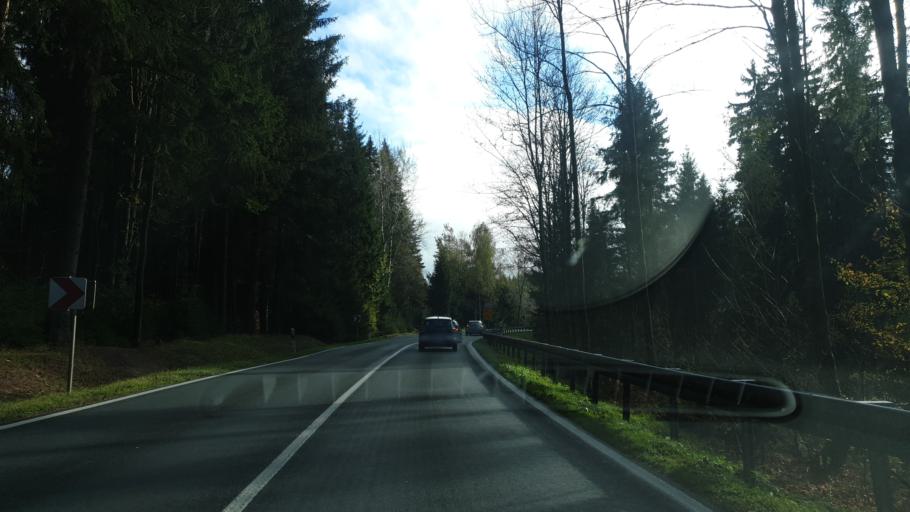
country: DE
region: Saxony
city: Eibenstock
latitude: 50.5107
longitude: 12.6098
